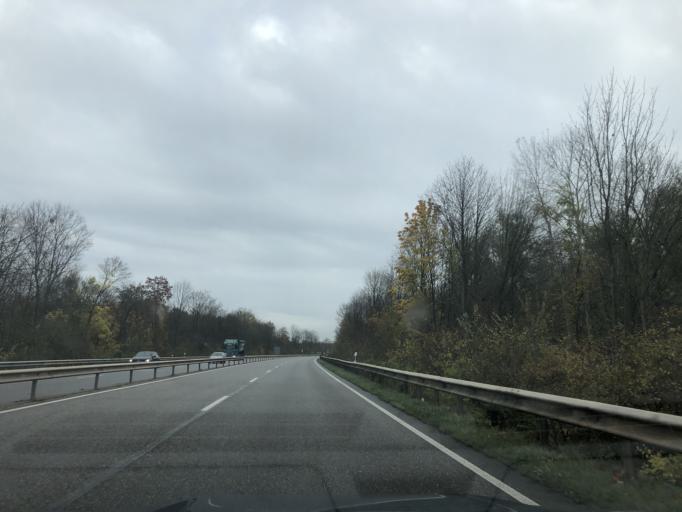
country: DE
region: Rheinland-Pfalz
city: Germersheim
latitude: 49.2246
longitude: 8.4069
